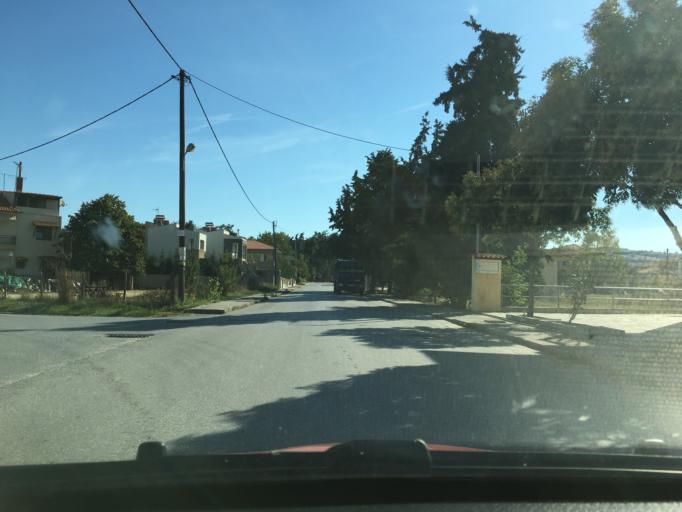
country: GR
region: Central Macedonia
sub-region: Nomos Chalkidikis
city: Ierissos
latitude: 40.3998
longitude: 23.8770
